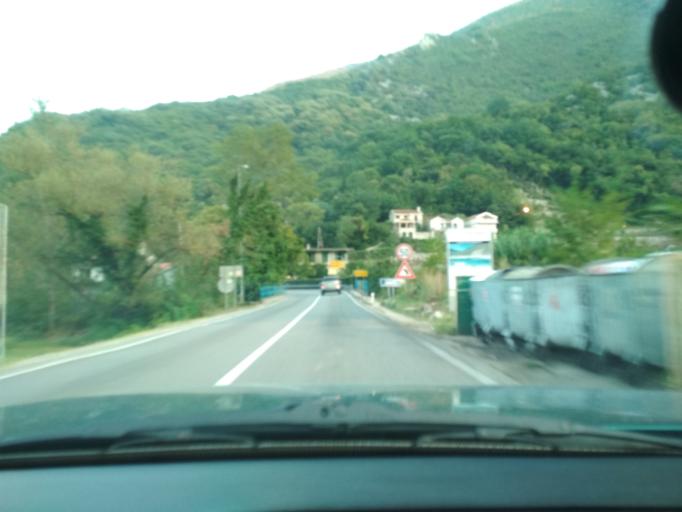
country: ME
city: Lipci
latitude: 42.4877
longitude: 18.6512
